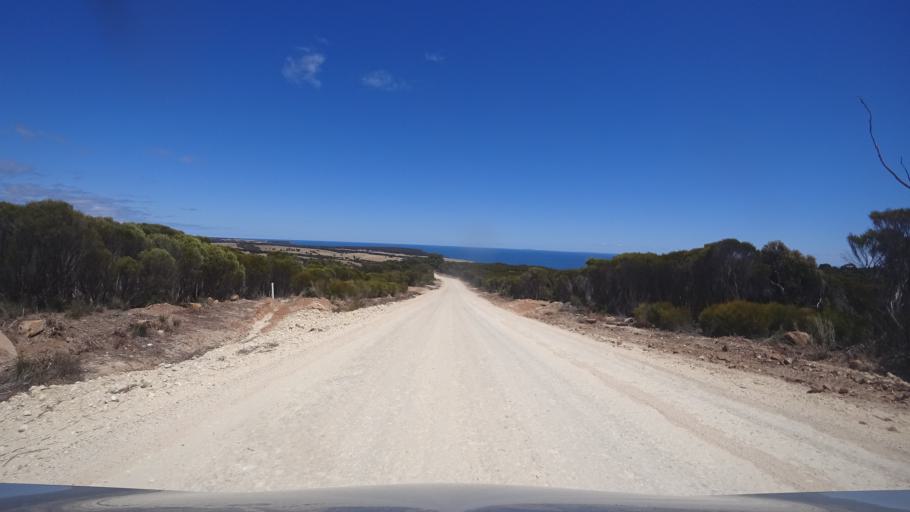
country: AU
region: South Australia
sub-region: Kangaroo Island
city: Kingscote
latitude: -35.6362
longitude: 137.2210
